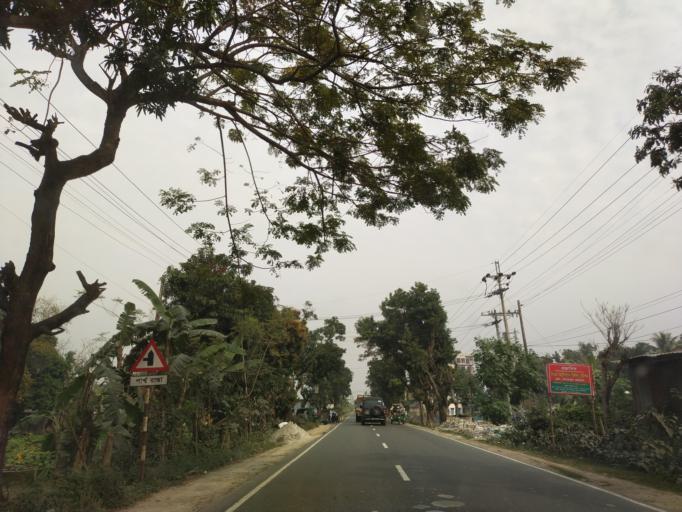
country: BD
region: Dhaka
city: Narsingdi
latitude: 23.9867
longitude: 90.7353
